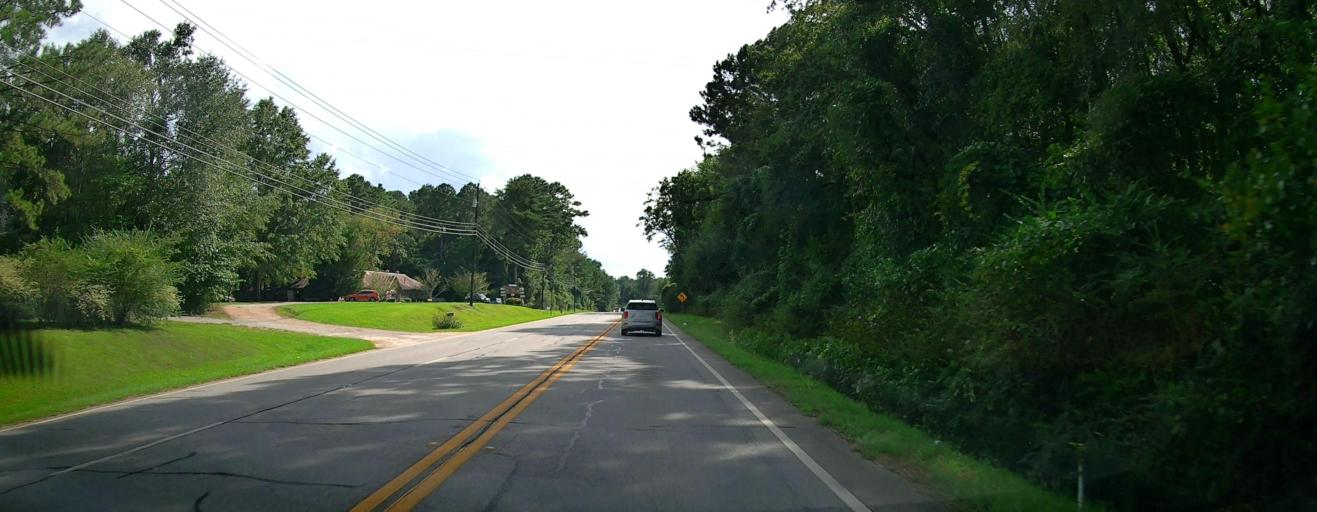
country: US
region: Georgia
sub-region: Harris County
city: Hamilton
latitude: 32.6144
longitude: -84.9088
